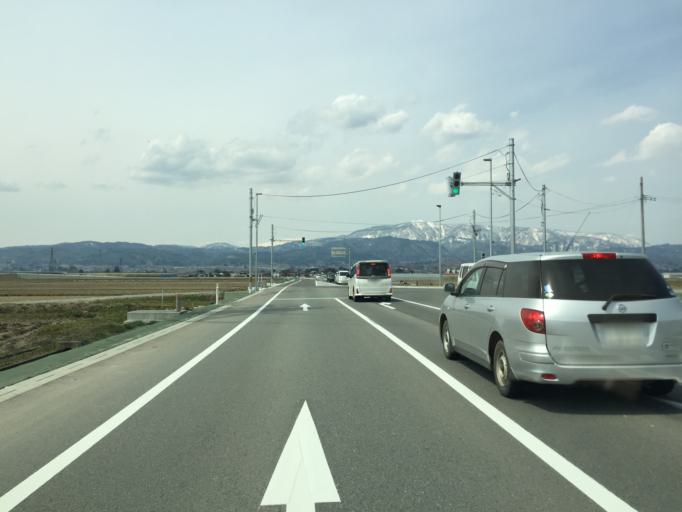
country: JP
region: Yamagata
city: Higashine
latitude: 38.4518
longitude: 140.3661
